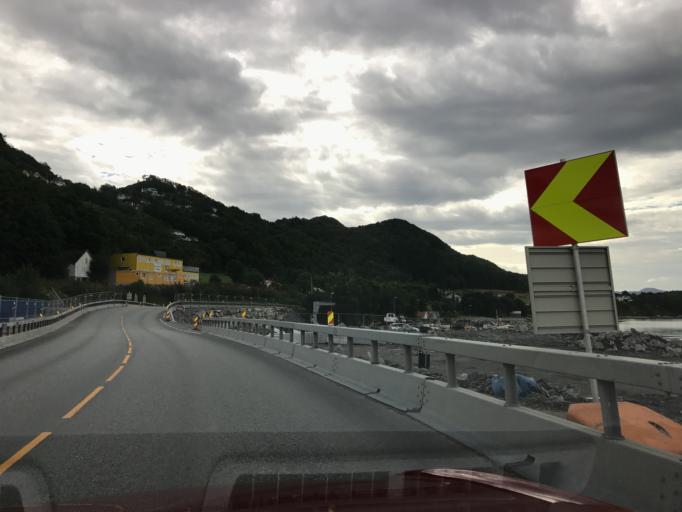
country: NO
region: Rogaland
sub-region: Strand
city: Tau
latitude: 59.0362
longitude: 5.9352
